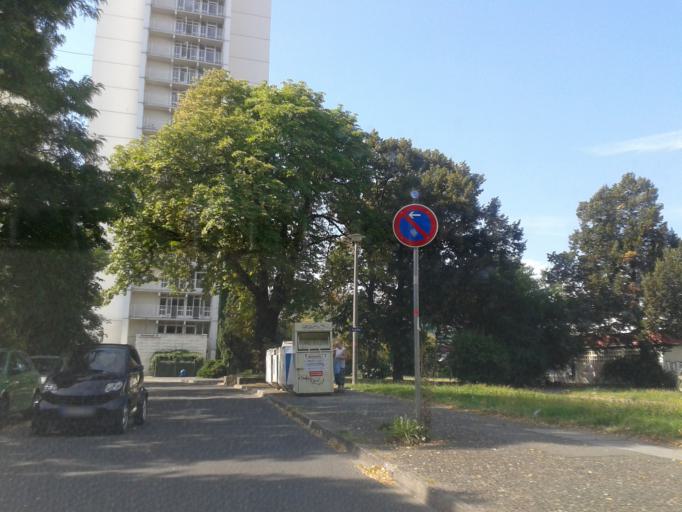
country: DE
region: Saxony
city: Dresden
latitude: 51.0346
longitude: 13.7868
